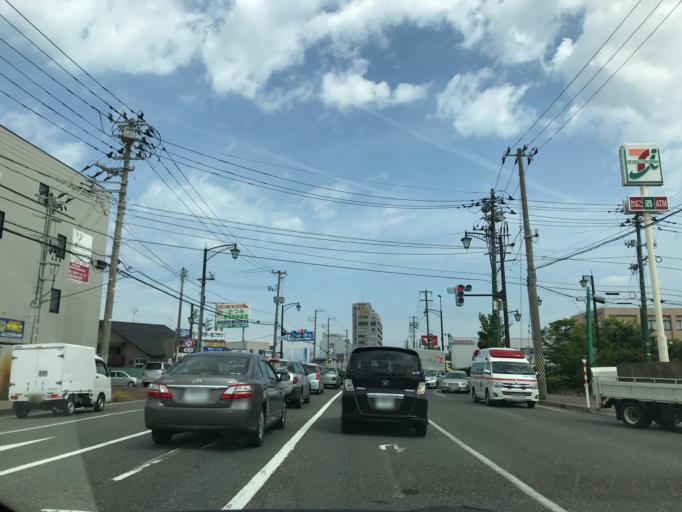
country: JP
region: Niigata
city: Niigata-shi
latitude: 37.8809
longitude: 139.0128
